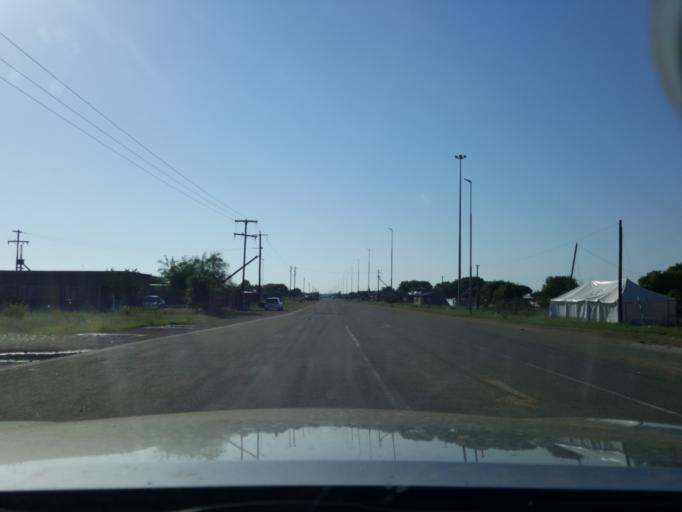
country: ZA
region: North-West
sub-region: Ngaka Modiri Molema District Municipality
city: Mmabatho
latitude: -25.8291
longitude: 25.6517
